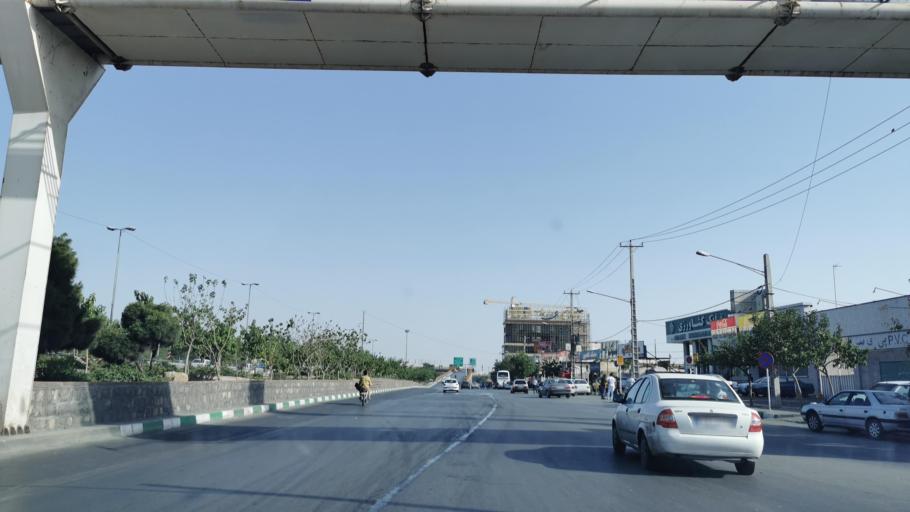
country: IR
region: Razavi Khorasan
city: Mashhad
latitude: 36.3665
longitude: 59.5365
